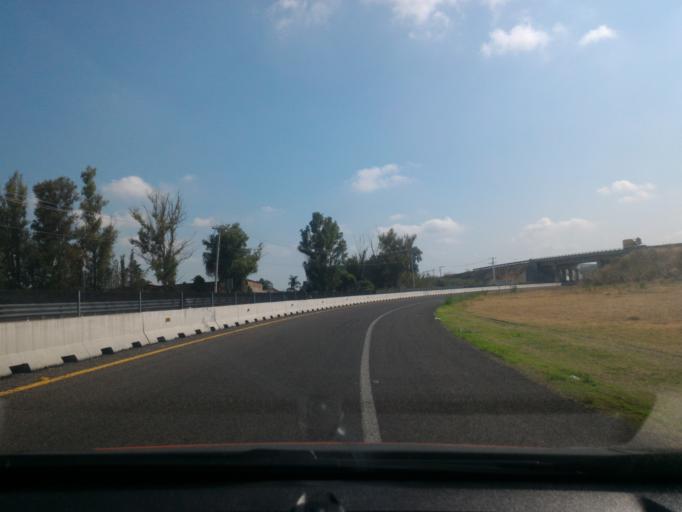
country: MX
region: Guanajuato
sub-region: Penjamo
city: Estacion la Piedad
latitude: 20.3933
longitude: -102.0008
